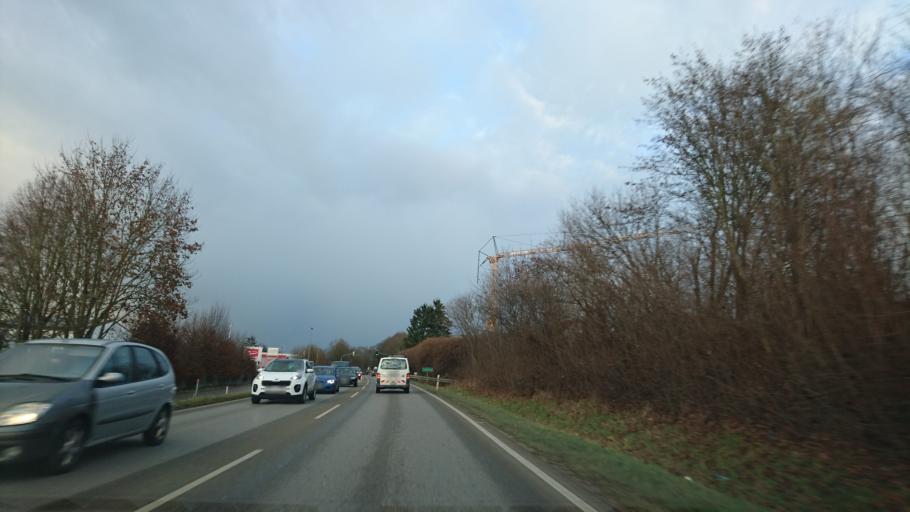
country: DE
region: Bavaria
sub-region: Swabia
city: Diedorf
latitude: 48.3654
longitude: 10.7928
